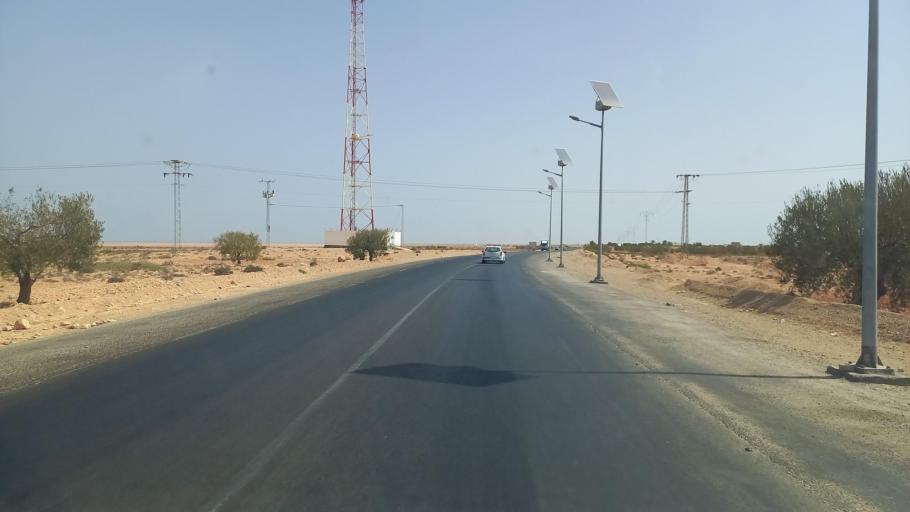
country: TN
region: Madanin
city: Medenine
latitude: 33.3857
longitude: 10.7026
